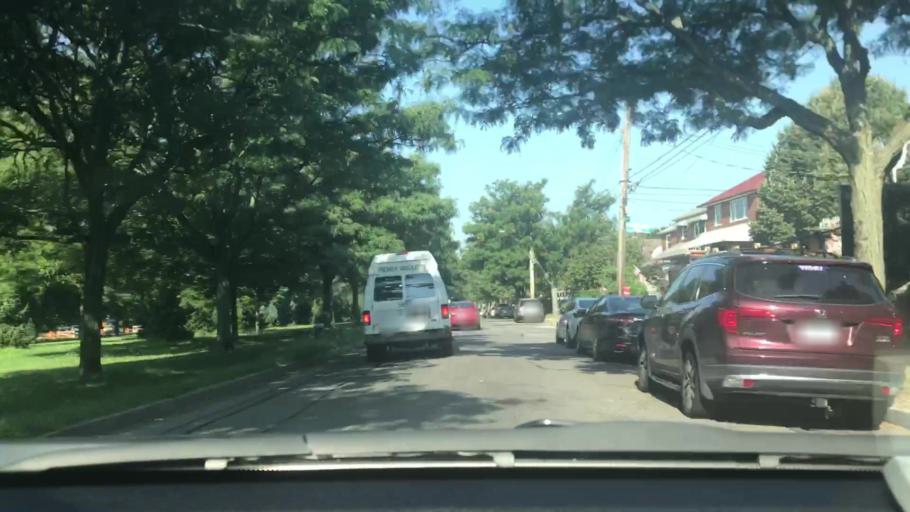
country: US
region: New York
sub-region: Bronx
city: The Bronx
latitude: 40.8577
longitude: -73.8393
